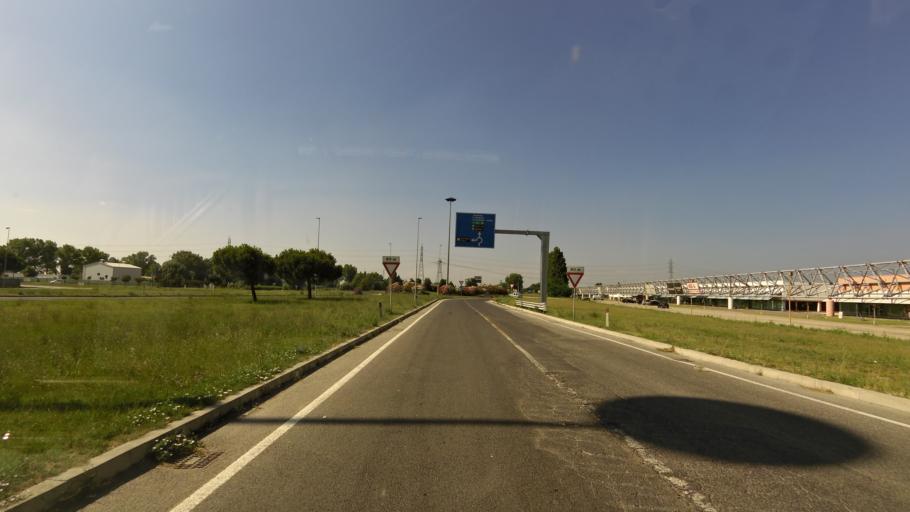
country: IT
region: Emilia-Romagna
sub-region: Provincia di Ravenna
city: Ravenna
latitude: 44.4491
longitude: 12.2100
